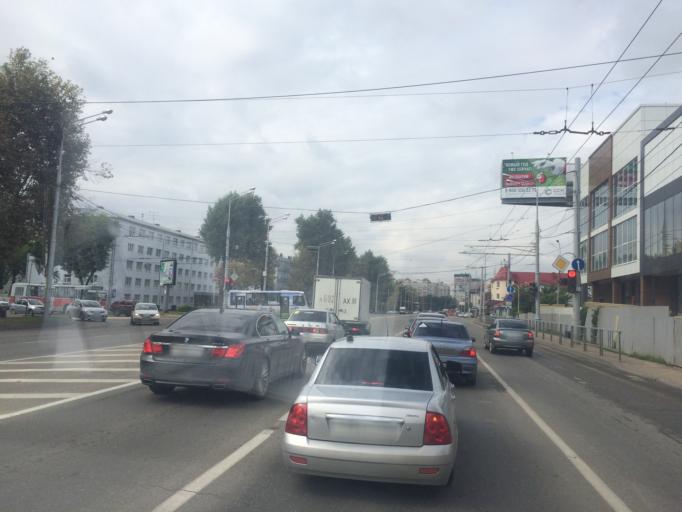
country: RU
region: Krasnodarskiy
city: Pashkovskiy
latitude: 45.0136
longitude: 39.0814
